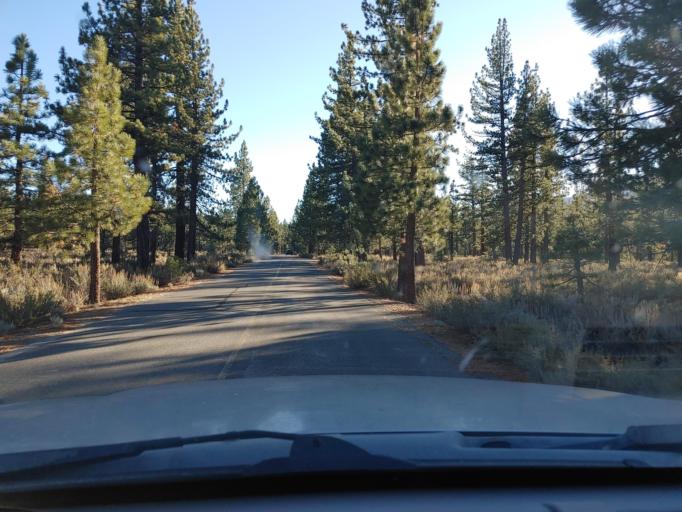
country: US
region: California
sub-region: El Dorado County
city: South Lake Tahoe
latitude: 38.9359
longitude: -120.0493
